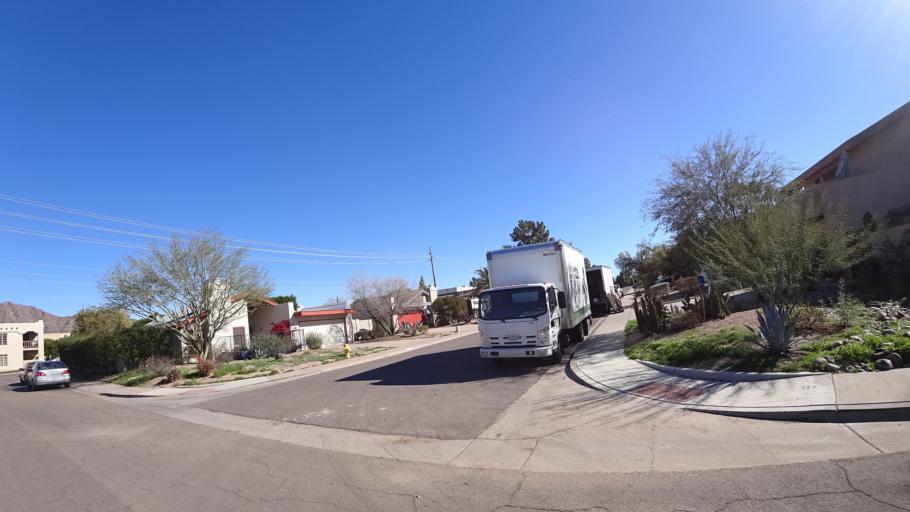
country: US
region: Arizona
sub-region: Maricopa County
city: Paradise Valley
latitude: 33.4777
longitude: -111.9638
